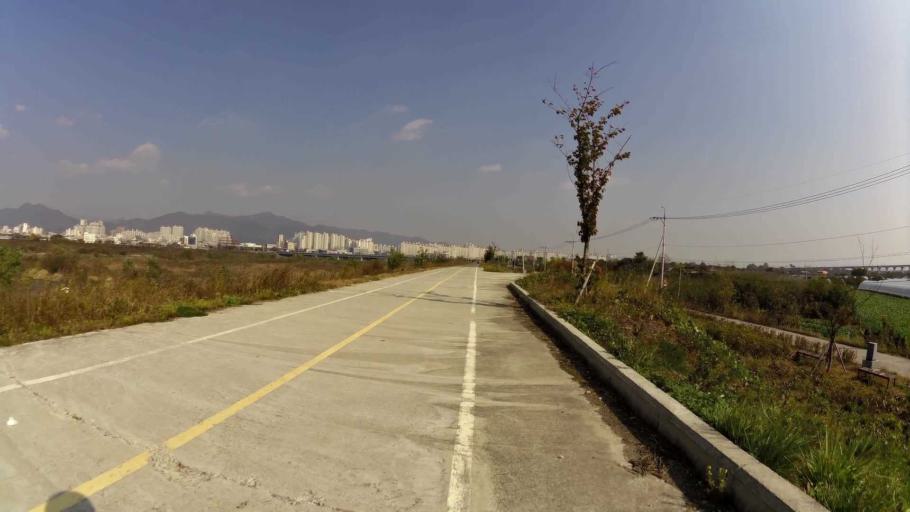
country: KR
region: Gyeongsangbuk-do
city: Gyeongsan-si
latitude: 35.8582
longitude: 128.7108
